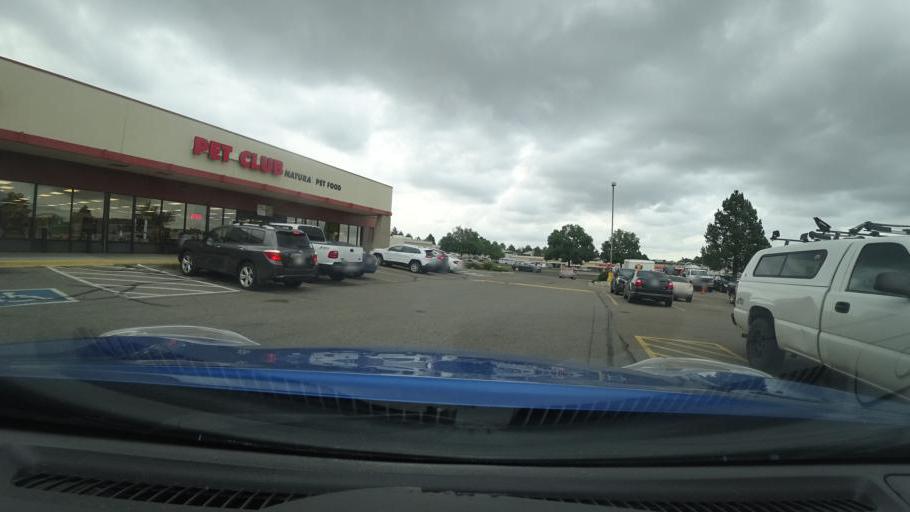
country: US
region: Colorado
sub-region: Adams County
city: Aurora
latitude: 39.6960
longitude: -104.8123
